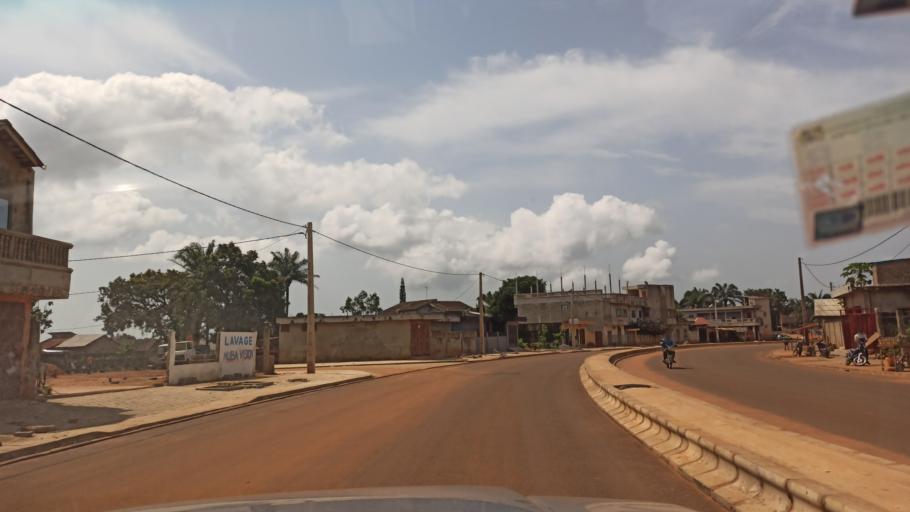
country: BJ
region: Queme
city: Porto-Novo
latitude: 6.4831
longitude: 2.5961
